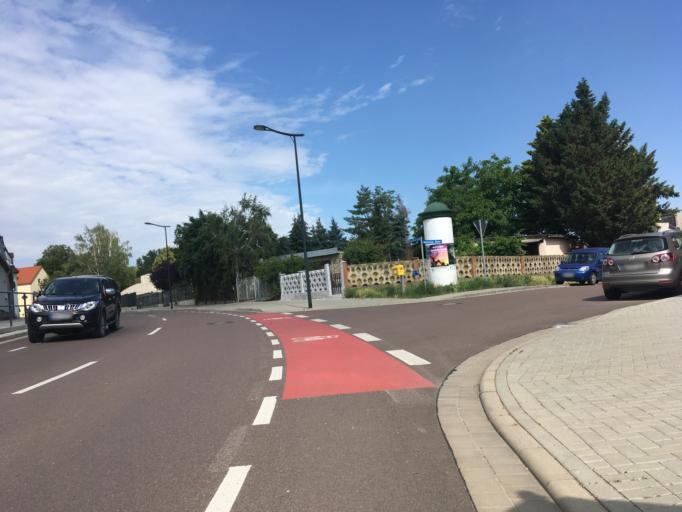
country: DE
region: Saxony-Anhalt
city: Bernburg
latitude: 51.7814
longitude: 11.7663
